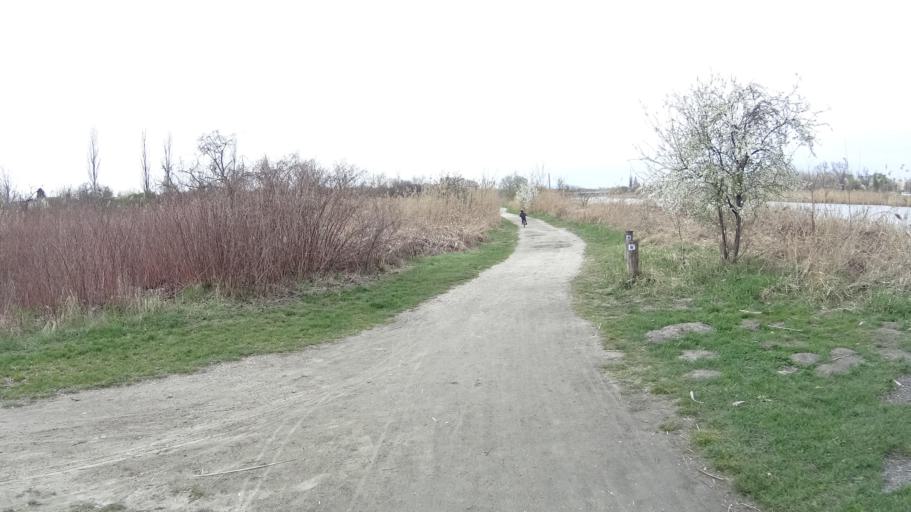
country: HU
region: Budapest
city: Budapest XX. keruelet
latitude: 47.4159
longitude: 19.0974
